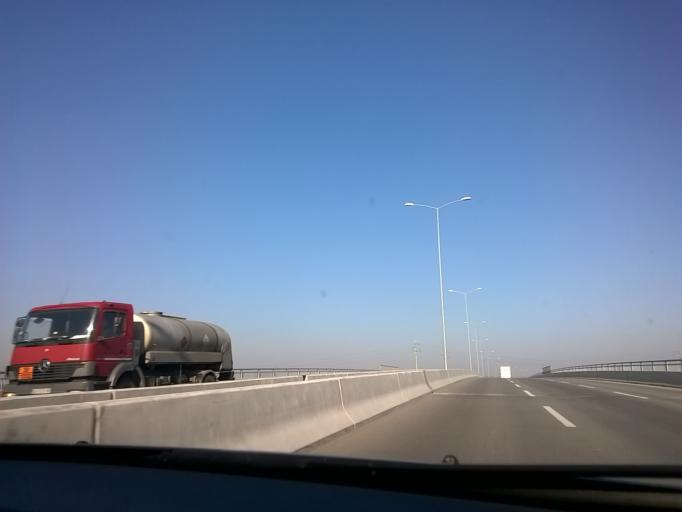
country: RS
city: Ovca
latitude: 44.8561
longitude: 20.5152
